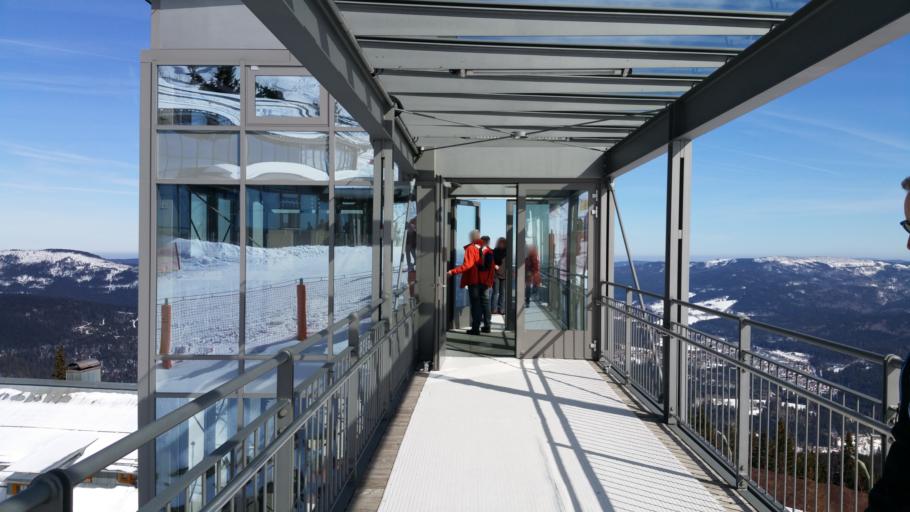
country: DE
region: Bavaria
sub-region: Lower Bavaria
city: Bodenmais
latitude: 49.1131
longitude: 13.1388
